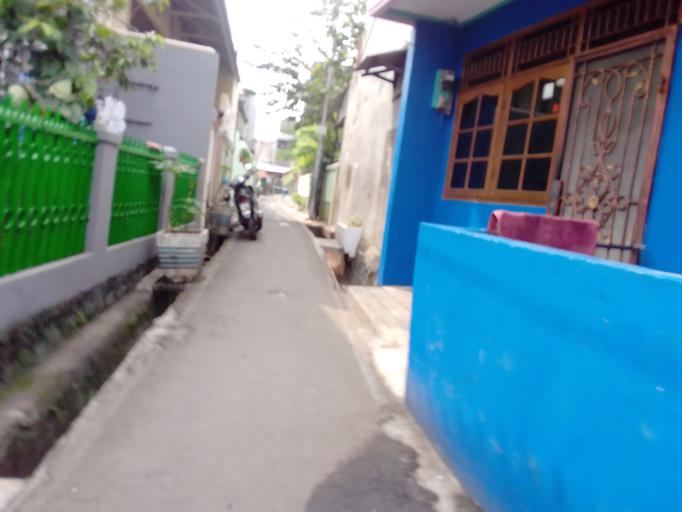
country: ID
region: Jakarta Raya
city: Jakarta
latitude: -6.1911
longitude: 106.8073
